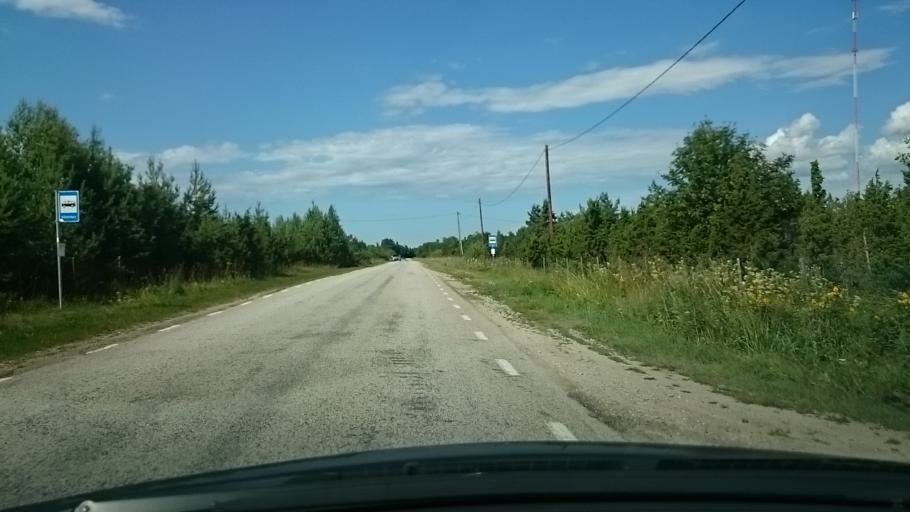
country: EE
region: Laeaene
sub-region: Haapsalu linn
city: Haapsalu
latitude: 59.1099
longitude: 23.5330
